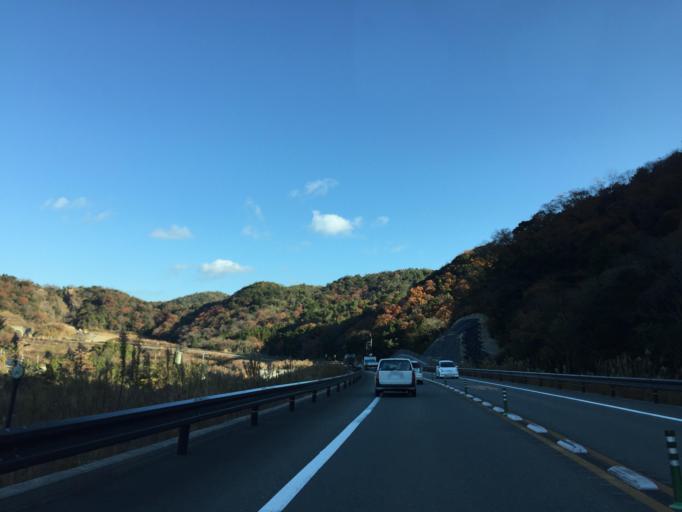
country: JP
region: Wakayama
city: Wakayama-shi
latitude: 34.3038
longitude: 135.1606
